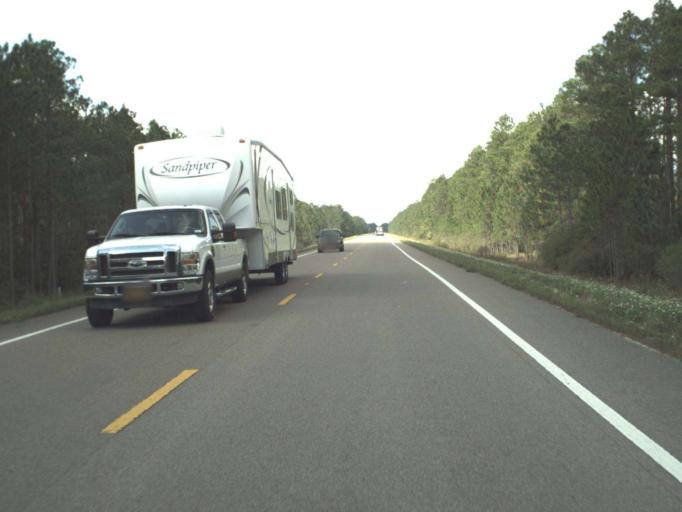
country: US
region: Florida
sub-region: Bay County
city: Laguna Beach
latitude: 30.4563
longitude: -85.9140
